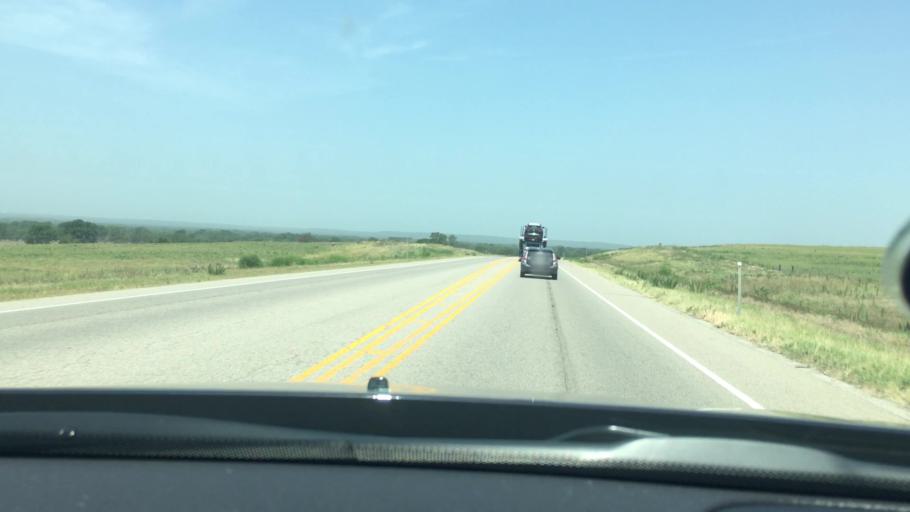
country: US
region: Oklahoma
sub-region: Pontotoc County
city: Ada
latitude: 34.6807
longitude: -96.5833
